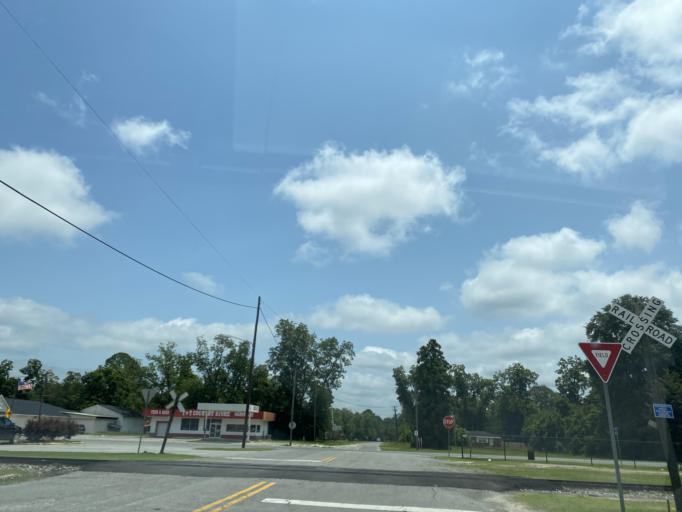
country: US
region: Georgia
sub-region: Wheeler County
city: Alamo
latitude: 32.1468
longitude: -82.7797
